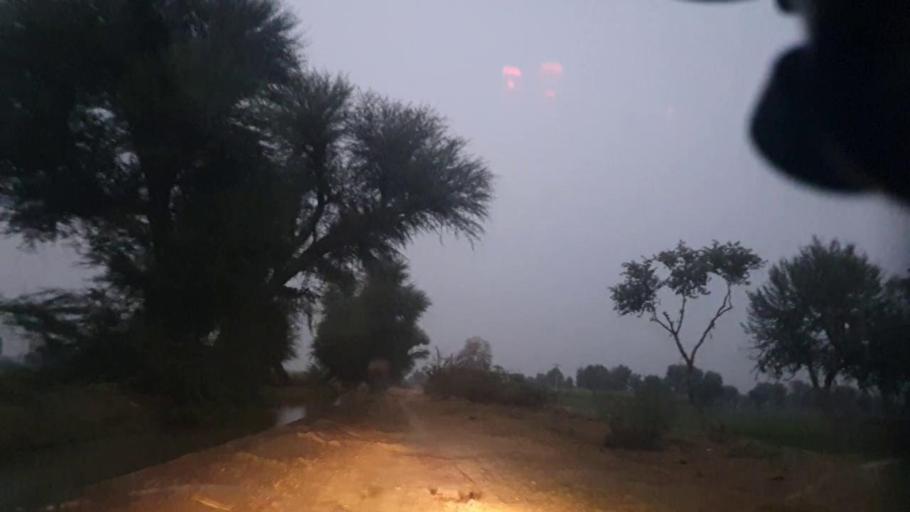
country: PK
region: Sindh
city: Hingorja
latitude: 27.2038
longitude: 68.3716
